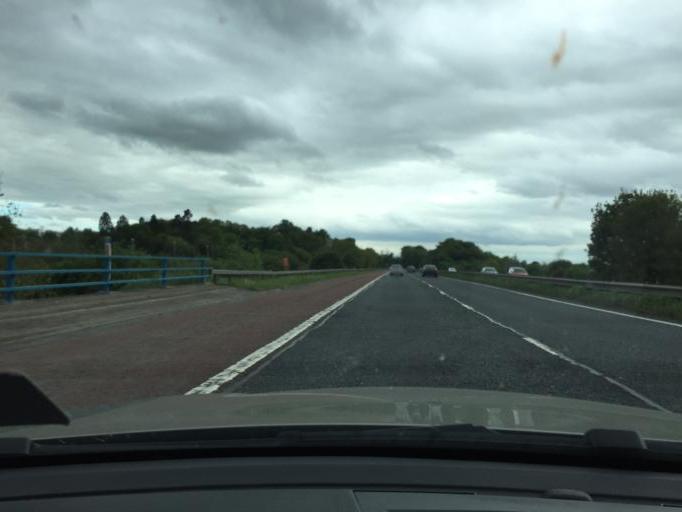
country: GB
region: Northern Ireland
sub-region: Lisburn District
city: Lisburn
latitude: 54.5577
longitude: -5.9953
